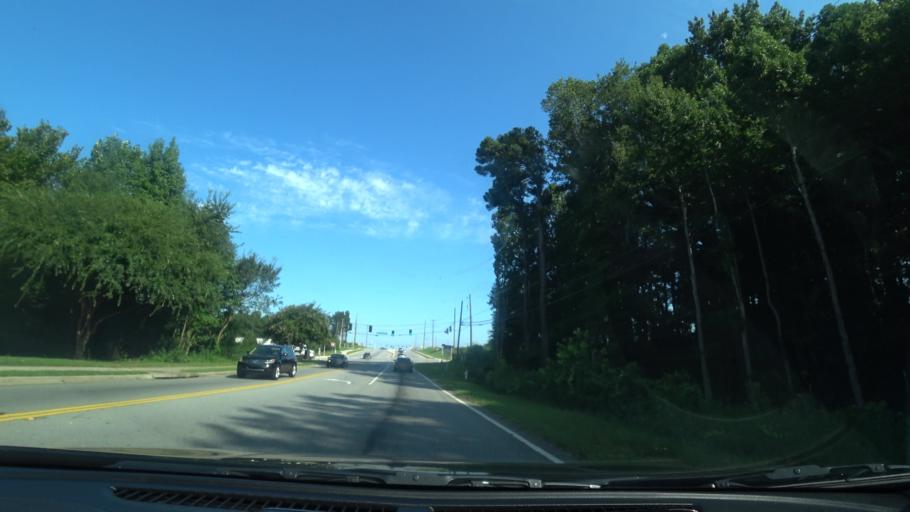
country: US
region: Georgia
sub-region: Gwinnett County
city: Lawrenceville
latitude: 33.9734
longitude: -83.9935
